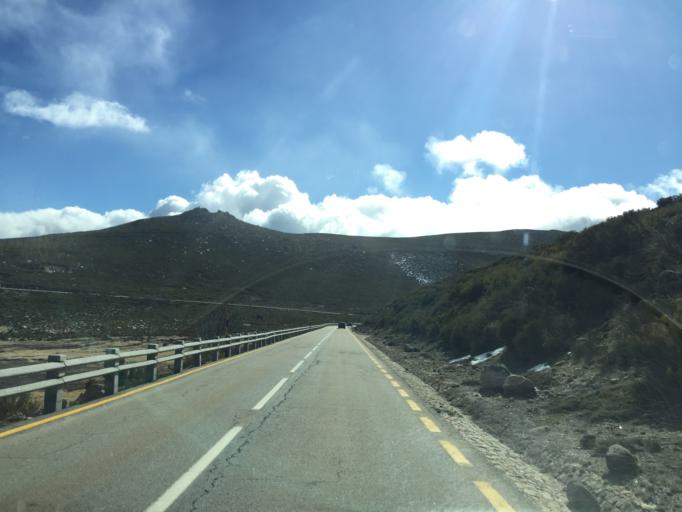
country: PT
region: Castelo Branco
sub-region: Covilha
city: Covilha
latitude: 40.3151
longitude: -7.5860
